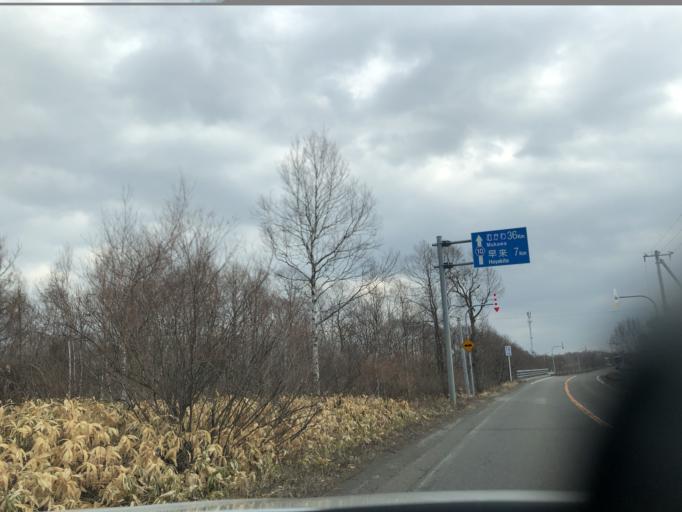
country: JP
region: Hokkaido
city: Chitose
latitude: 42.7661
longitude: 141.7179
